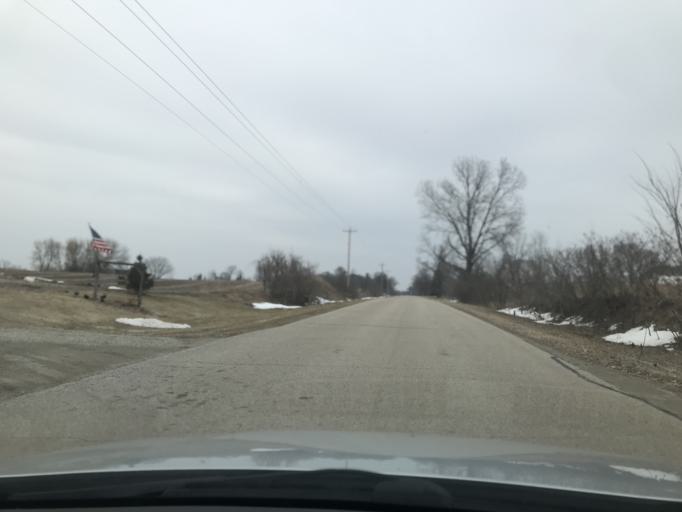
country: US
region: Wisconsin
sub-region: Marinette County
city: Peshtigo
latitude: 45.0399
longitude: -87.8602
